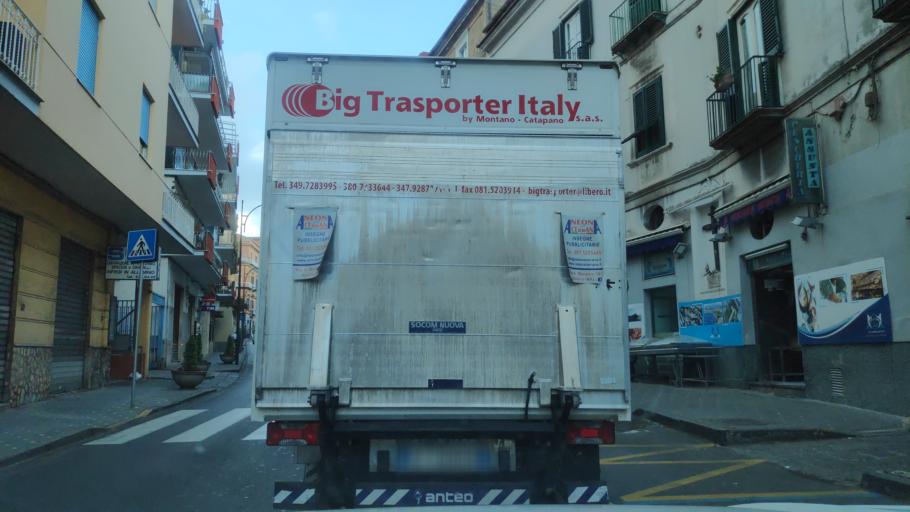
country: IT
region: Campania
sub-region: Provincia di Napoli
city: Meta
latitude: 40.6383
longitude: 14.4187
